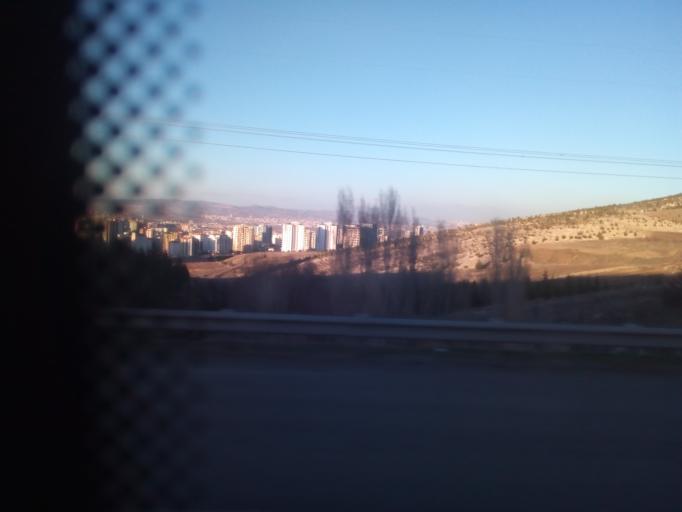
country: TR
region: Ankara
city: Etimesgut
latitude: 39.8782
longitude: 32.6296
